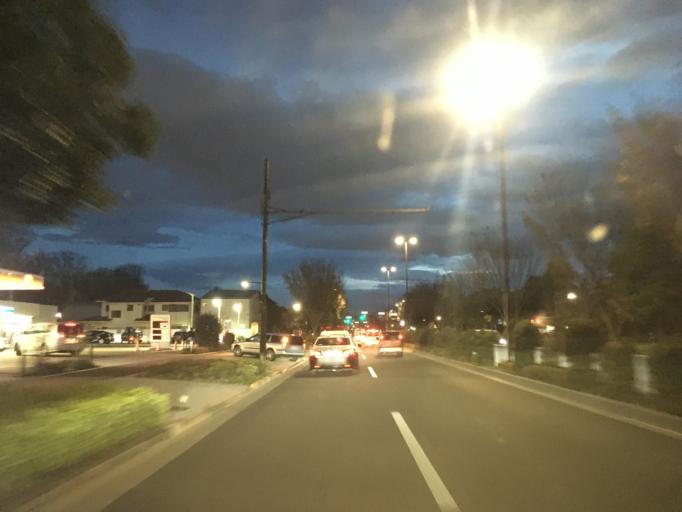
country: JP
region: Tokyo
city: Chofugaoka
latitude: 35.6742
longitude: 139.5455
